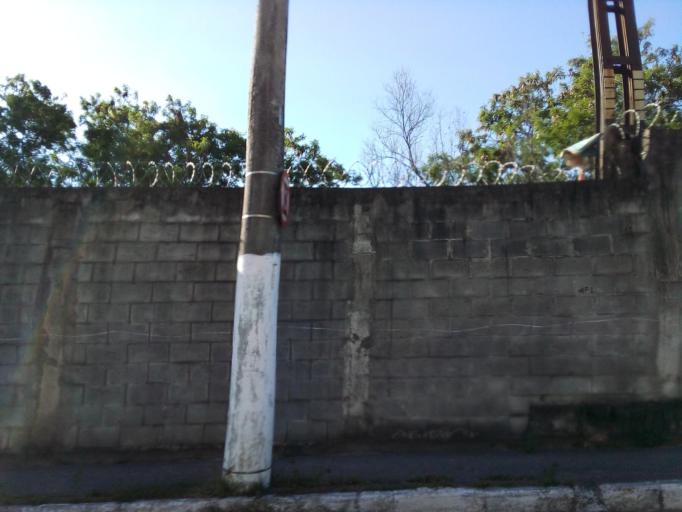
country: BR
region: Espirito Santo
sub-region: Vitoria
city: Vitoria
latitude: -20.3264
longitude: -40.3439
